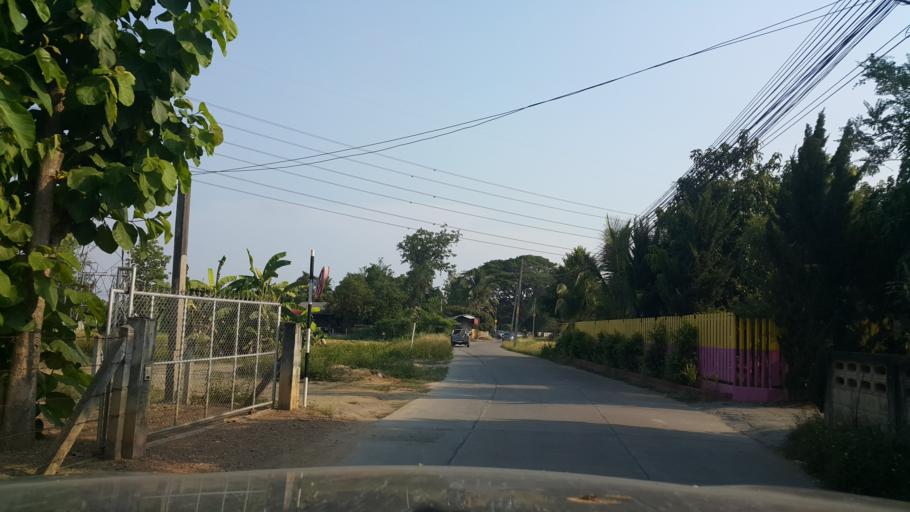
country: TH
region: Chiang Mai
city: Saraphi
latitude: 18.7232
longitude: 98.9738
